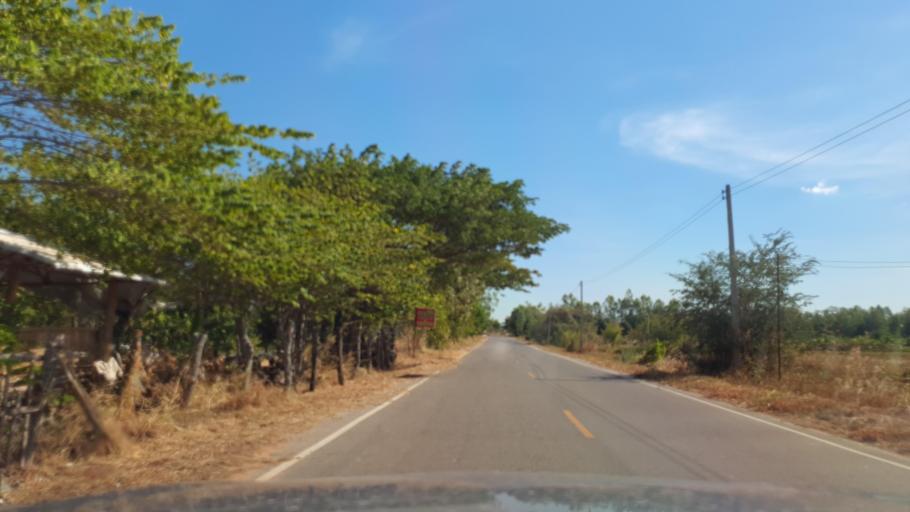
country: TH
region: Kalasin
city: Khao Wong
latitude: 16.7298
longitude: 104.0980
